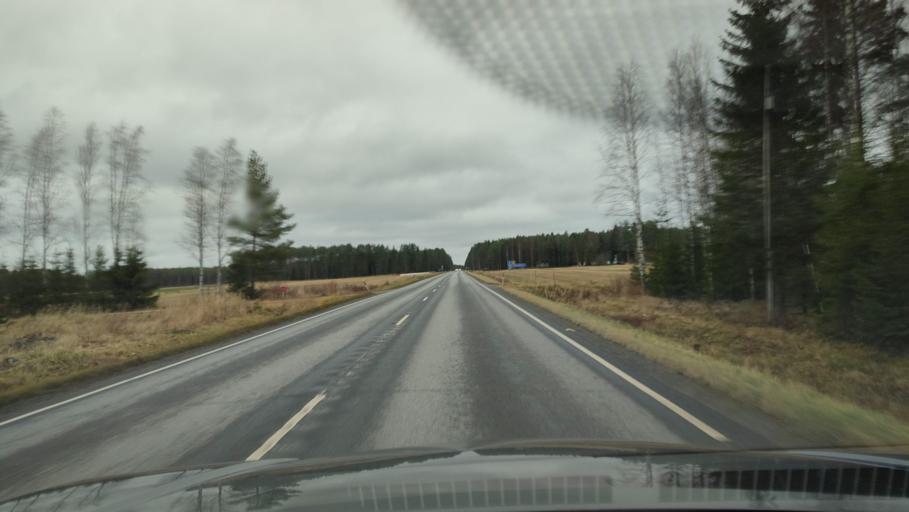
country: FI
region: Southern Ostrobothnia
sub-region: Suupohja
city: Kauhajoki
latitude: 62.5027
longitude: 22.3035
